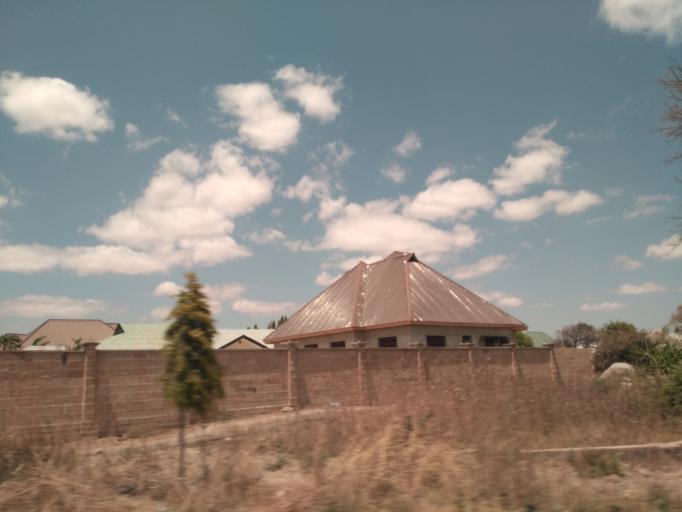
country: TZ
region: Dodoma
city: Kisasa
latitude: -6.1652
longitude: 35.7979
